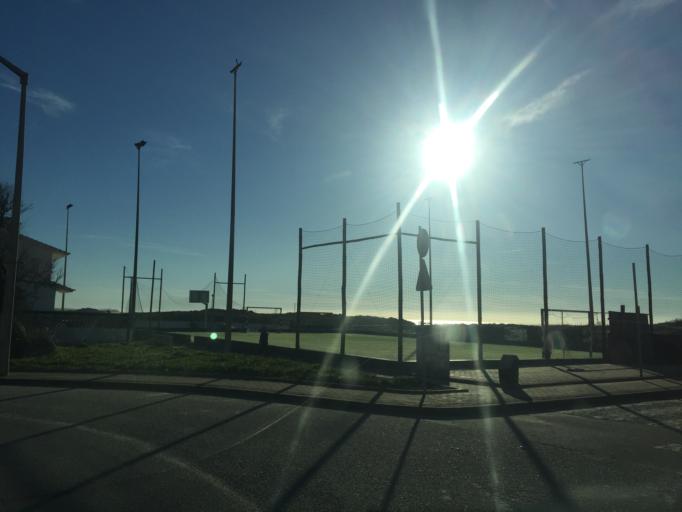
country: PT
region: Coimbra
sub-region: Figueira da Foz
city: Lavos
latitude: 40.0895
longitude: -8.8753
